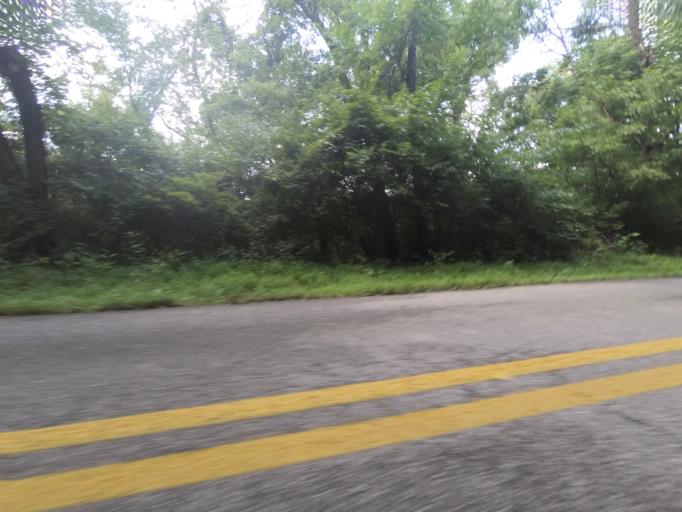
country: US
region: West Virginia
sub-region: Cabell County
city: Barboursville
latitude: 38.4173
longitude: -82.2951
